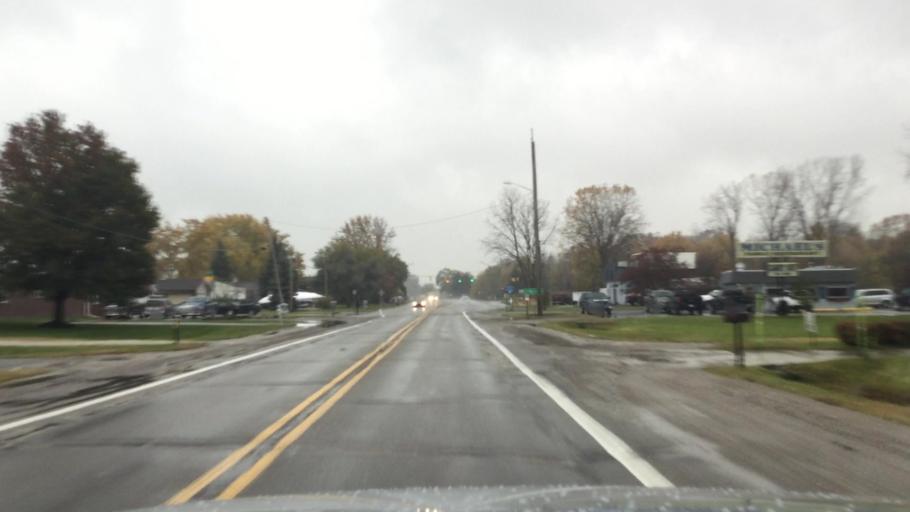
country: US
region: Michigan
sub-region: Macomb County
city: Mount Clemens
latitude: 42.6440
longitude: -82.8146
